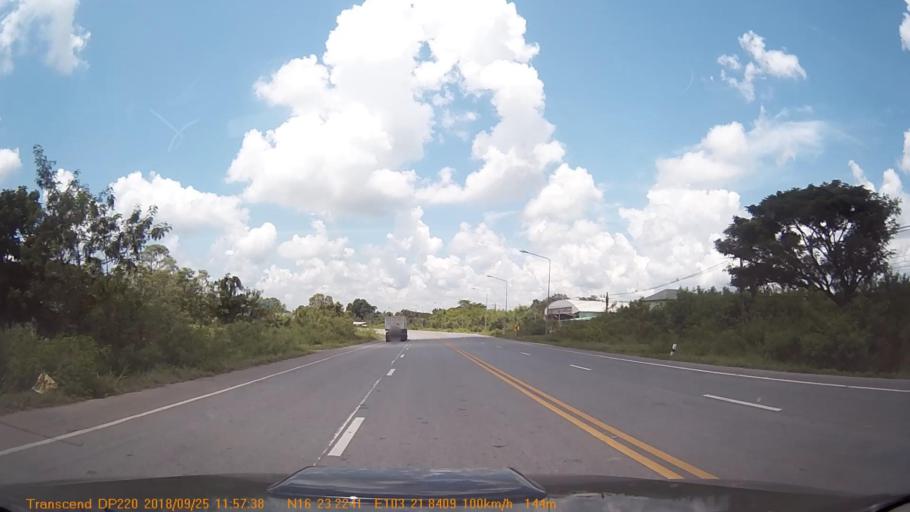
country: TH
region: Kalasin
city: Yang Talat
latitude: 16.3871
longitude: 103.3640
